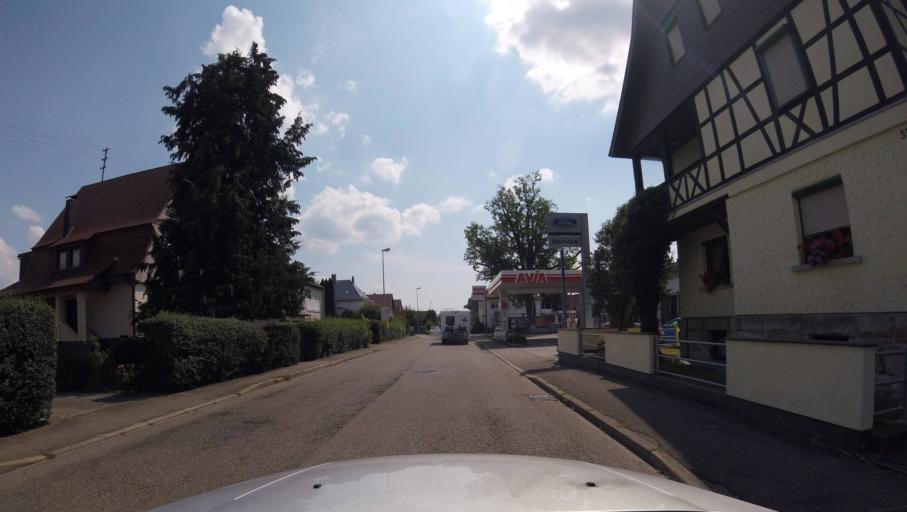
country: DE
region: Baden-Wuerttemberg
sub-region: Regierungsbezirk Stuttgart
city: Welzheim
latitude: 48.8802
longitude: 9.6339
